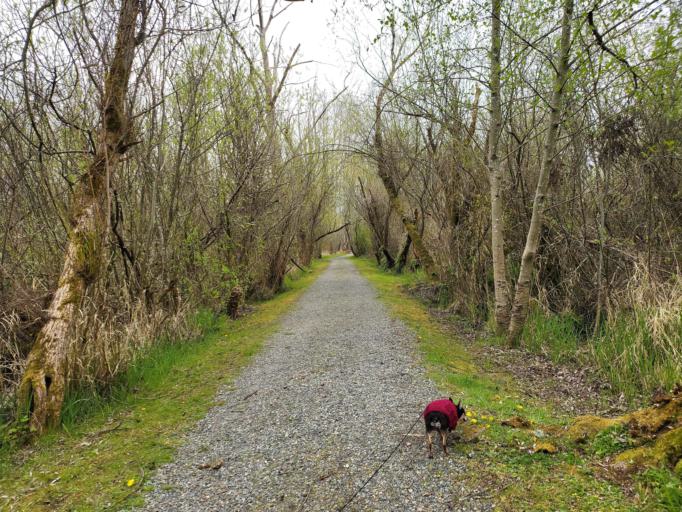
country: US
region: Washington
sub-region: King County
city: Newport
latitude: 47.5883
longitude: -122.1893
